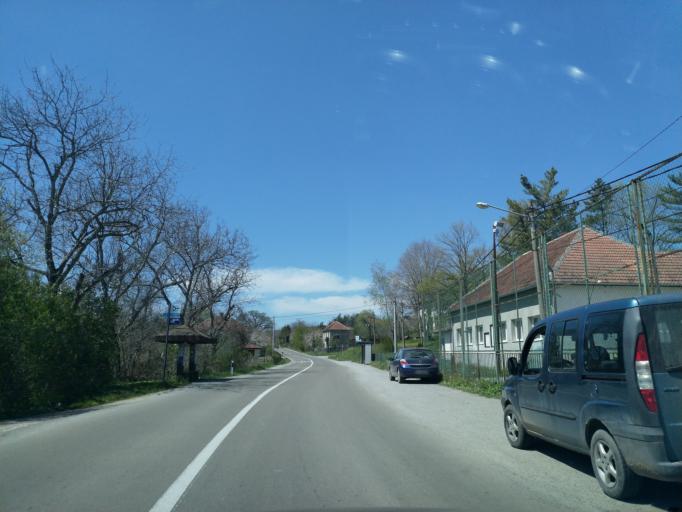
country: RS
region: Central Serbia
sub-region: Belgrade
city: Lazarevac
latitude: 44.3532
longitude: 20.3732
